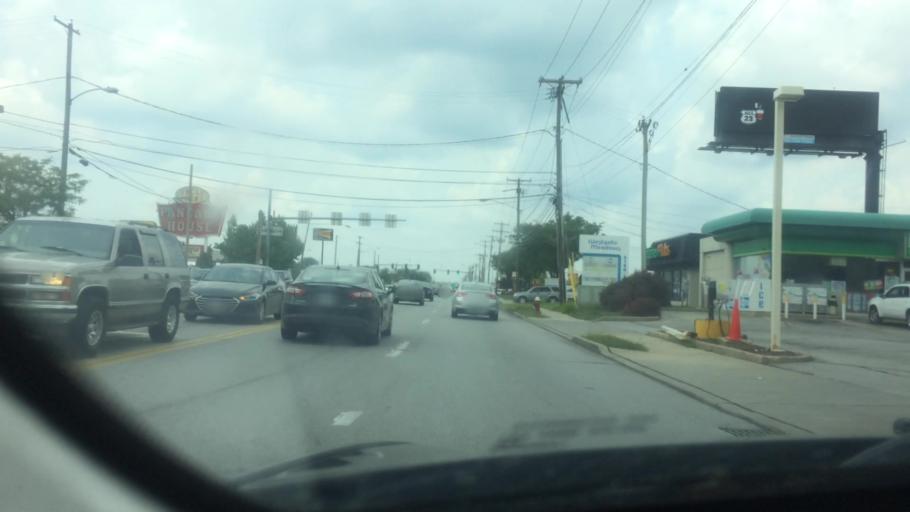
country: US
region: Ohio
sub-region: Lucas County
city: Ottawa Hills
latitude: 41.6775
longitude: -83.6226
